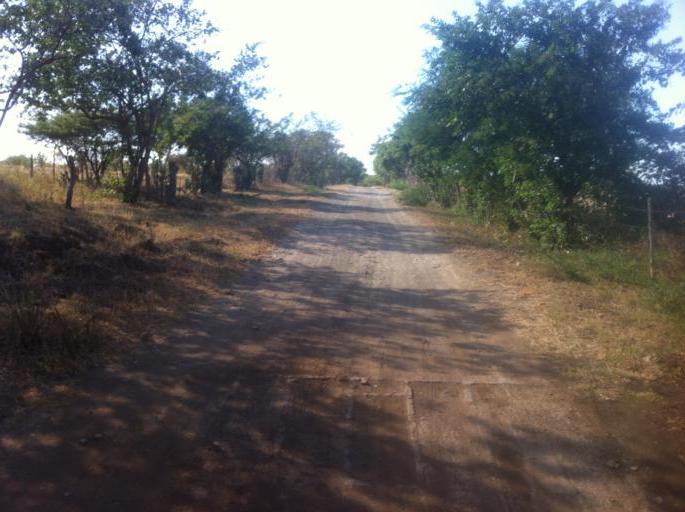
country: NI
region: Managua
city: Carlos Fonseca Amador
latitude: 11.9087
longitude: -86.6067
